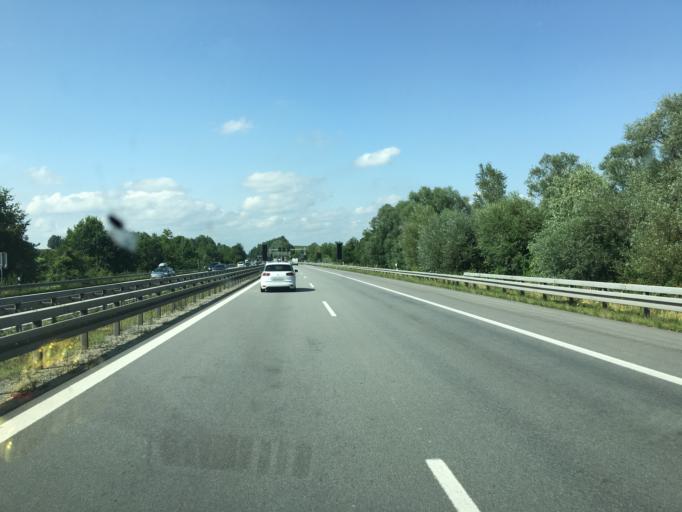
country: AT
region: Upper Austria
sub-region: Politischer Bezirk Scharding
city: Scharding
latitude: 48.4510
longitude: 13.3762
